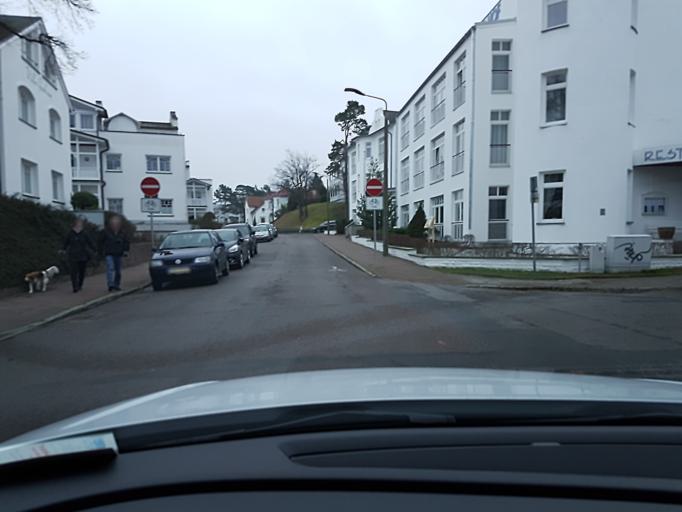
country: DE
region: Mecklenburg-Vorpommern
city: Ostseebad Binz
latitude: 54.4052
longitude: 13.6071
